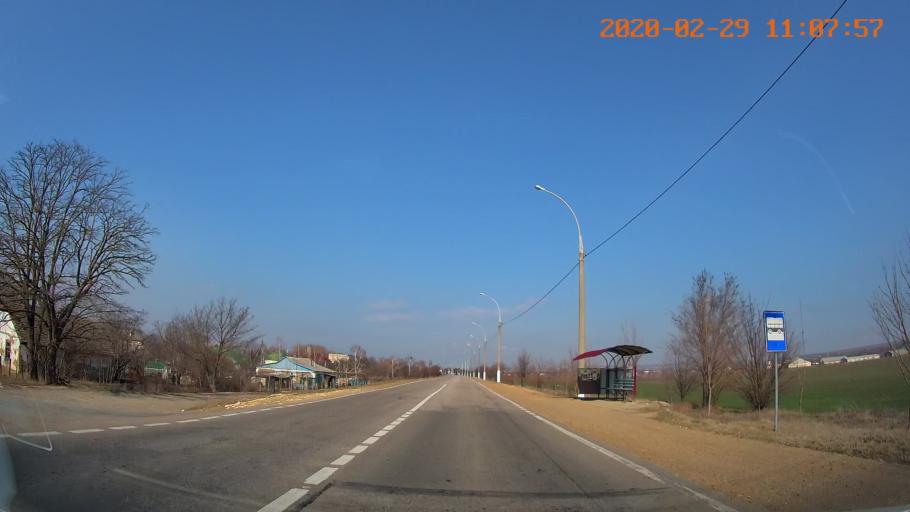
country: MD
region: Criuleni
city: Criuleni
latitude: 47.2297
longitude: 29.1788
